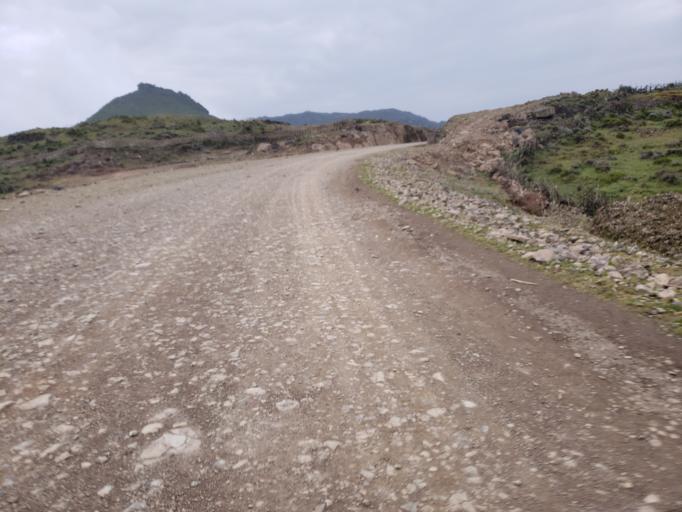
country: ET
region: Oromiya
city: Dodola
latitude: 6.7304
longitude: 39.4281
